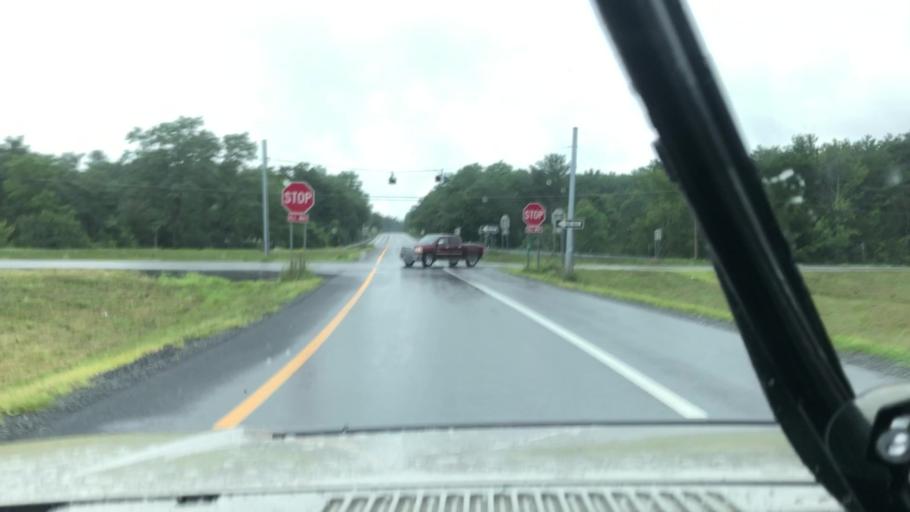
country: US
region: New York
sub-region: Greene County
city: Cairo
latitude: 42.3082
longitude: -74.0132
